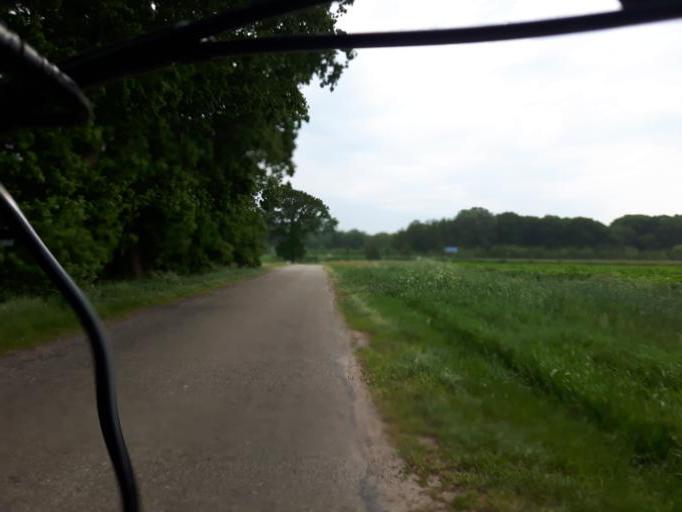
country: NL
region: North Brabant
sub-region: Gemeente Bergen op Zoom
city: Lepelstraat
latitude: 51.5328
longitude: 4.3068
